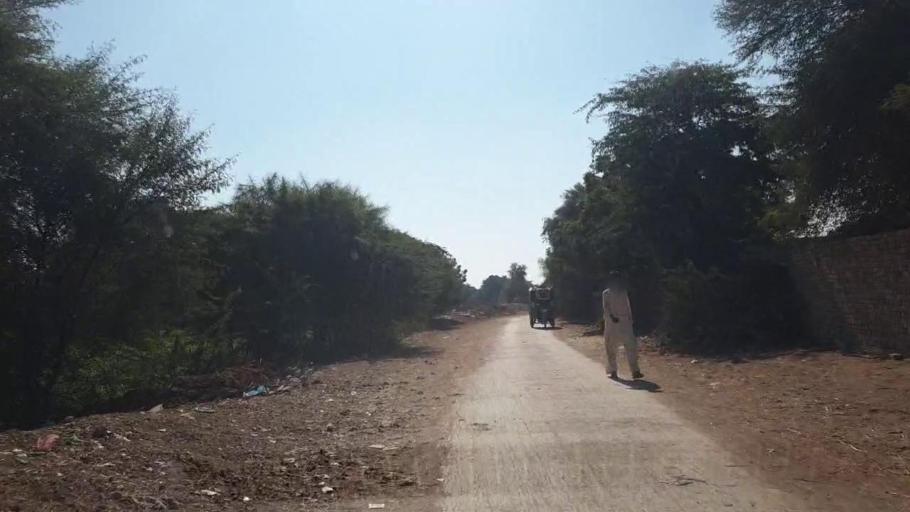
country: PK
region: Sindh
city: Shahpur Chakar
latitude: 26.1071
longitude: 68.6359
